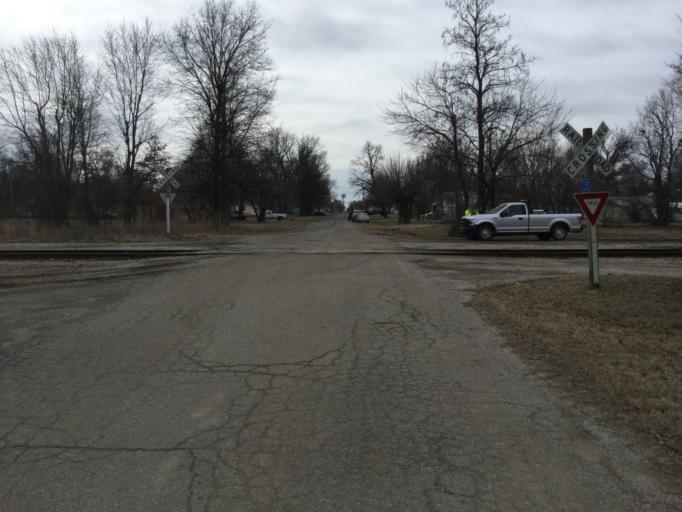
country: US
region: Kansas
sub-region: Cherokee County
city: Columbus
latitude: 37.1753
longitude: -94.8413
